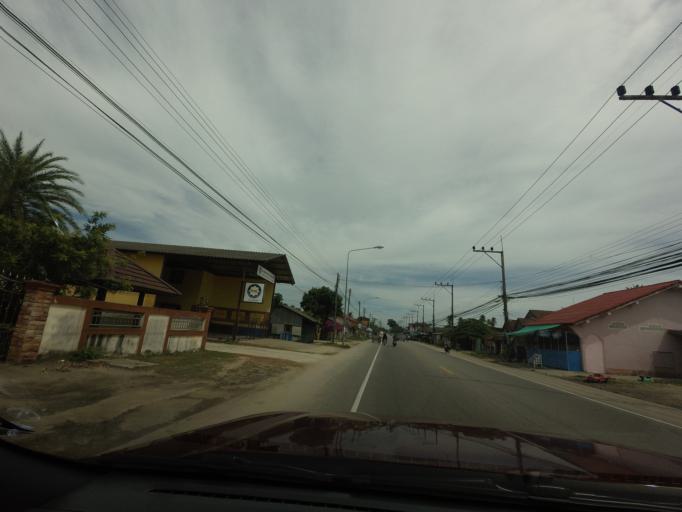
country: TH
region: Narathiwat
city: Tak Bai
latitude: 6.2511
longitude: 102.0659
